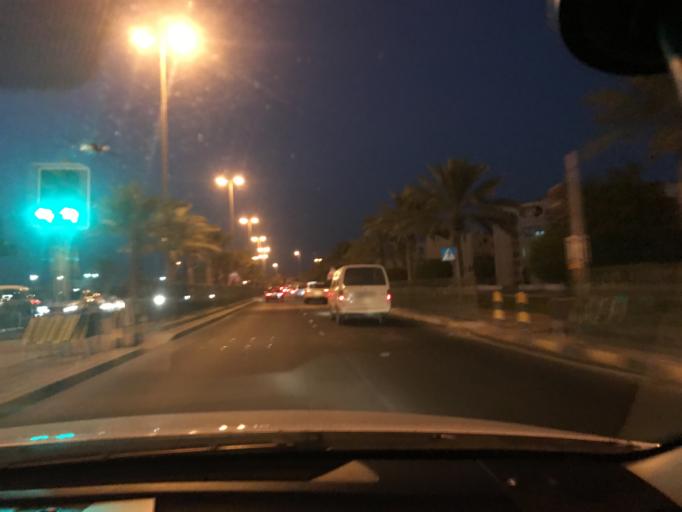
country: BH
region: Muharraq
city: Al Muharraq
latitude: 26.2637
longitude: 50.6034
